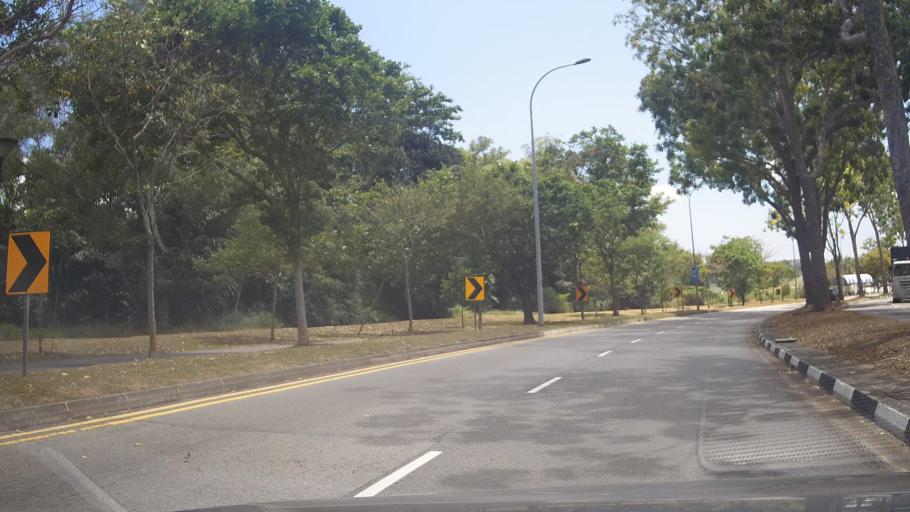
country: MY
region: Johor
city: Kampung Pasir Gudang Baru
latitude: 1.3745
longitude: 103.9633
